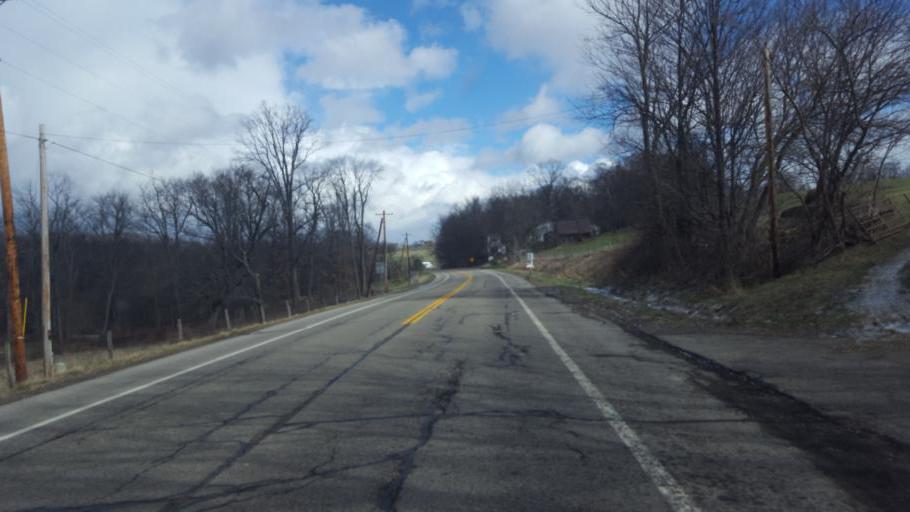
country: US
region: Ohio
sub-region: Tuscarawas County
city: Sugarcreek
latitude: 40.4388
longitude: -81.7433
